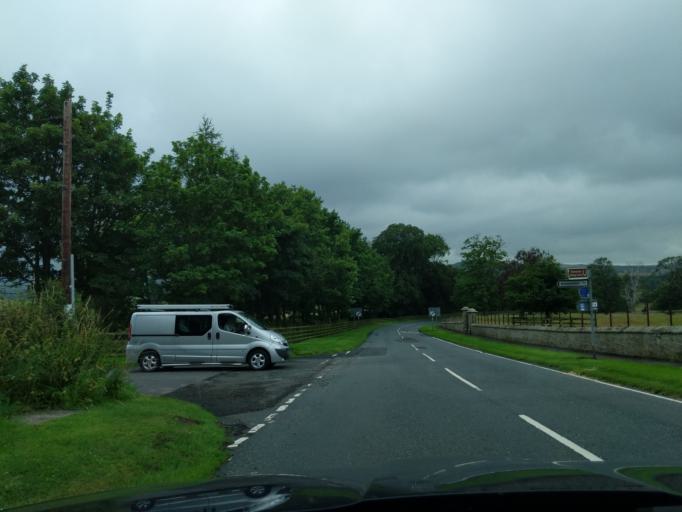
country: GB
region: England
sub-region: Northumberland
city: Ford
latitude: 55.6292
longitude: -2.0895
